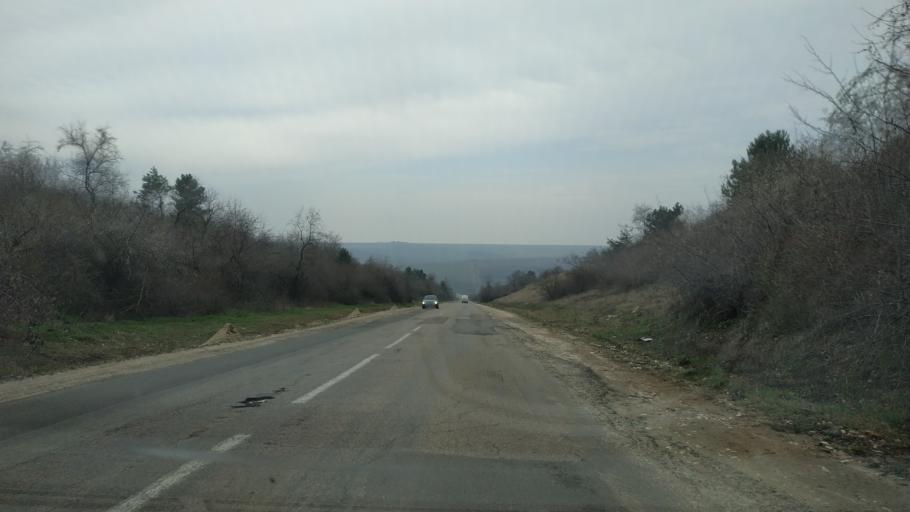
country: MD
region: Cahul
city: Cahul
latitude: 45.9570
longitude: 28.3633
